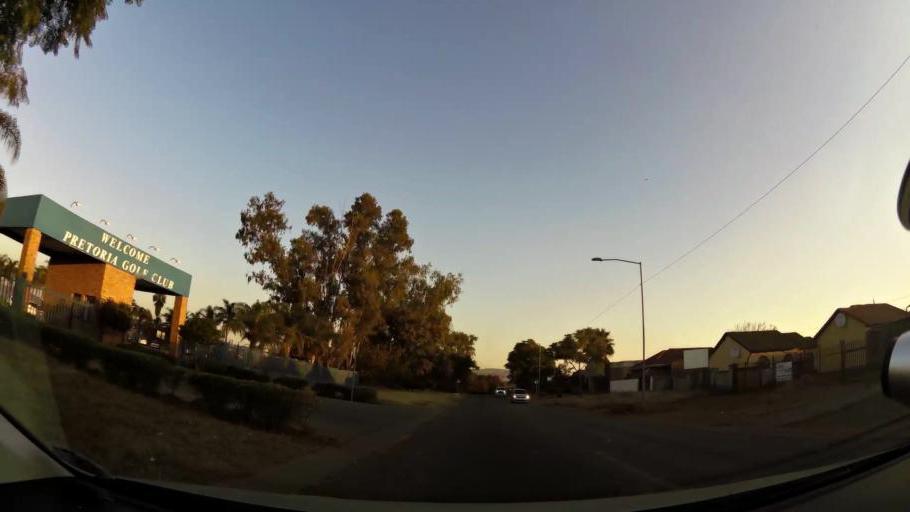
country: ZA
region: Gauteng
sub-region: City of Tshwane Metropolitan Municipality
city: Pretoria
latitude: -25.7392
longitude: 28.1416
